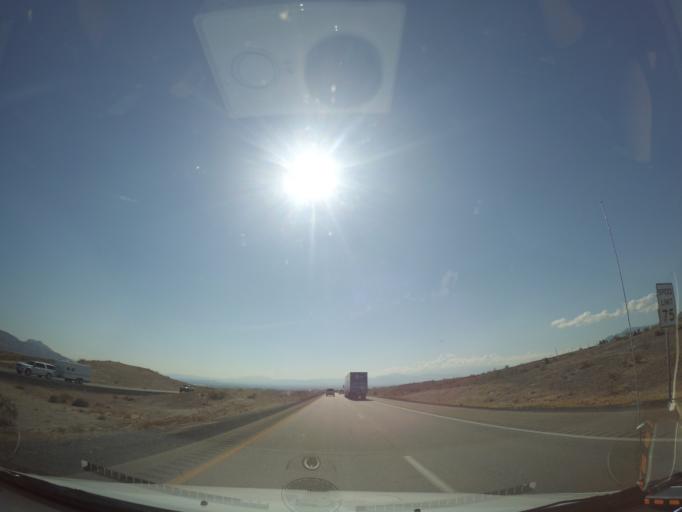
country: US
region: Nevada
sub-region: Clark County
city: Nellis Air Force Base
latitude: 36.3071
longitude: -114.9618
